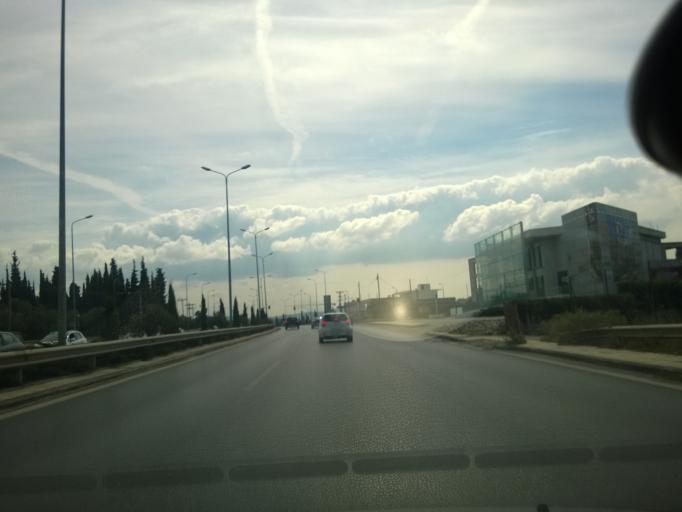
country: GR
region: Central Macedonia
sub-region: Nomos Thessalonikis
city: Kalamaria
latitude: 40.5604
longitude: 22.9766
